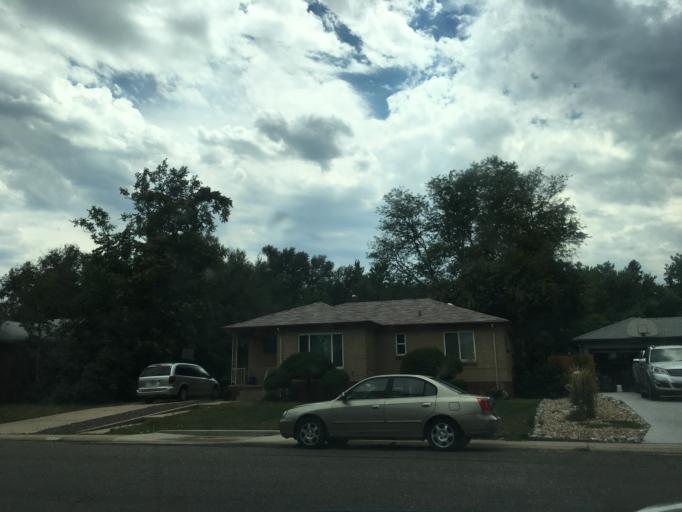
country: US
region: Colorado
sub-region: Arapahoe County
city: Sheridan
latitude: 39.6712
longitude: -105.0482
